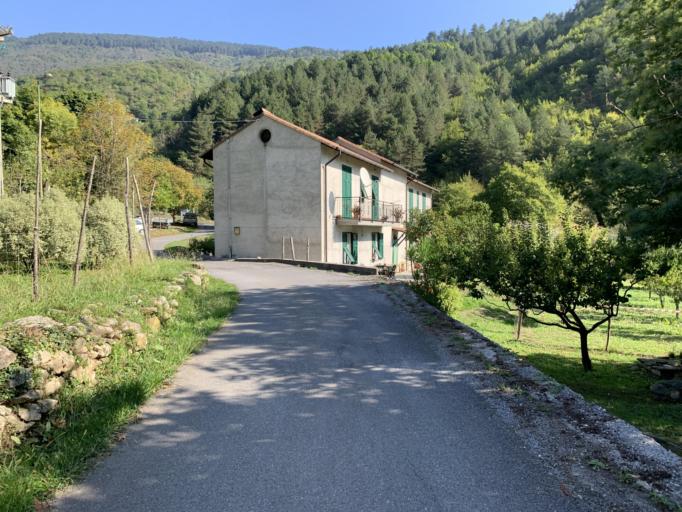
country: IT
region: Liguria
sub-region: Provincia di Savona
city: Magliolo
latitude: 44.2032
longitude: 8.2203
